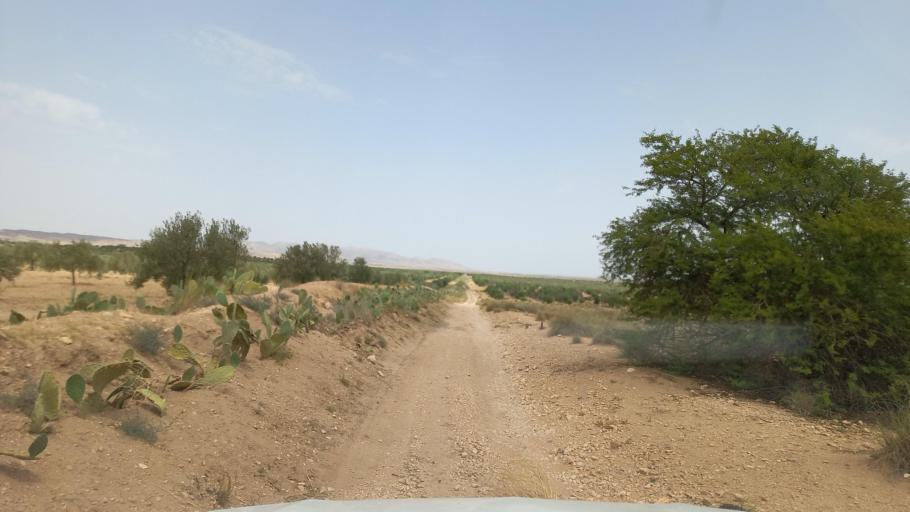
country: TN
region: Al Qasrayn
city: Kasserine
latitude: 35.2935
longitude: 9.0046
